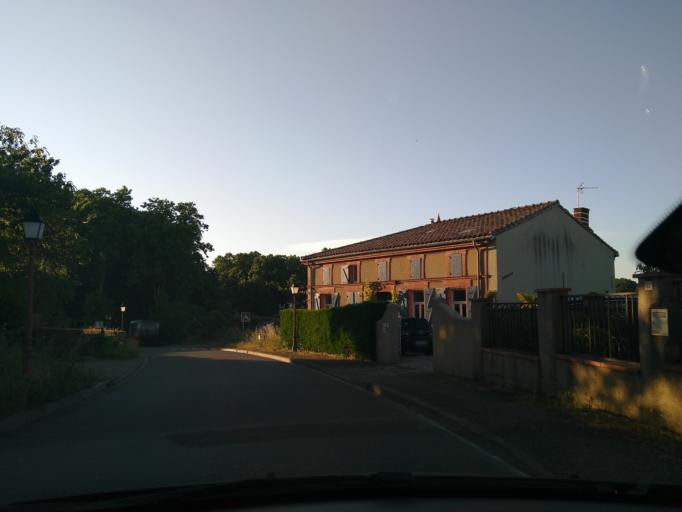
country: FR
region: Midi-Pyrenees
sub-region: Departement de la Haute-Garonne
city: Merville
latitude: 43.7186
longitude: 1.2997
